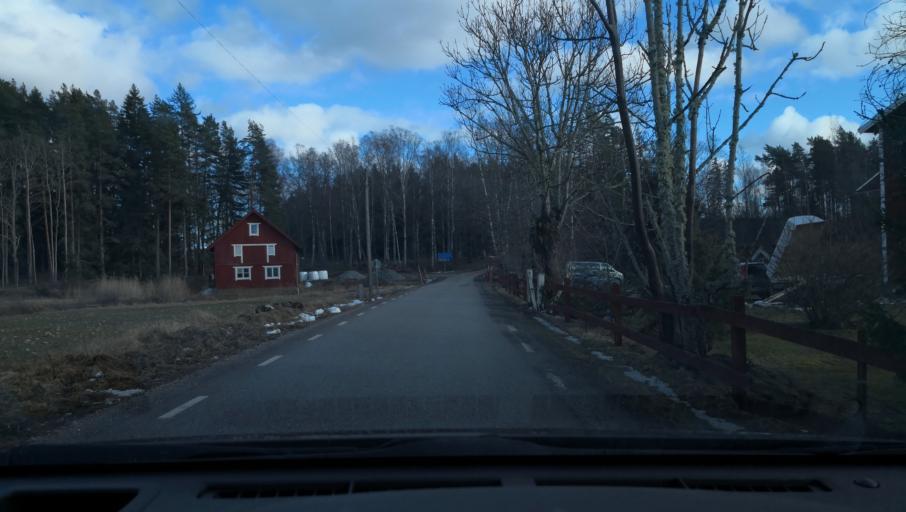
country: SE
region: Vaestmanland
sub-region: Arboga Kommun
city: Arboga
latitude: 59.3166
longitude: 15.7650
